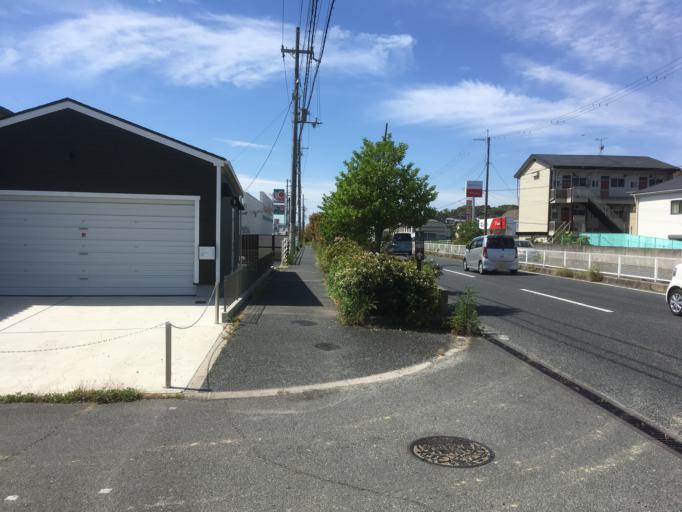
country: JP
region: Nara
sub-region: Ikoma-shi
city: Ikoma
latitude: 34.6806
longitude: 135.7062
